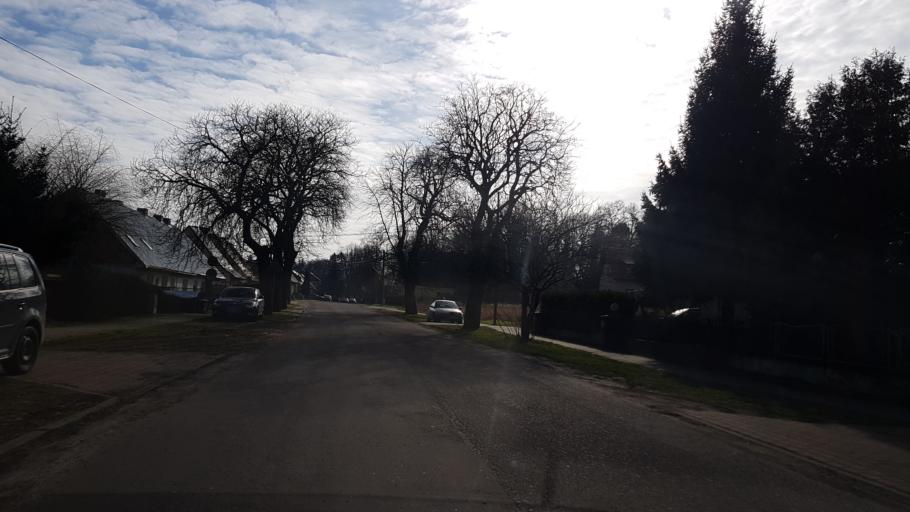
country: PL
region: West Pomeranian Voivodeship
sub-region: Powiat policki
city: Dobra
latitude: 53.5595
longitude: 14.3157
